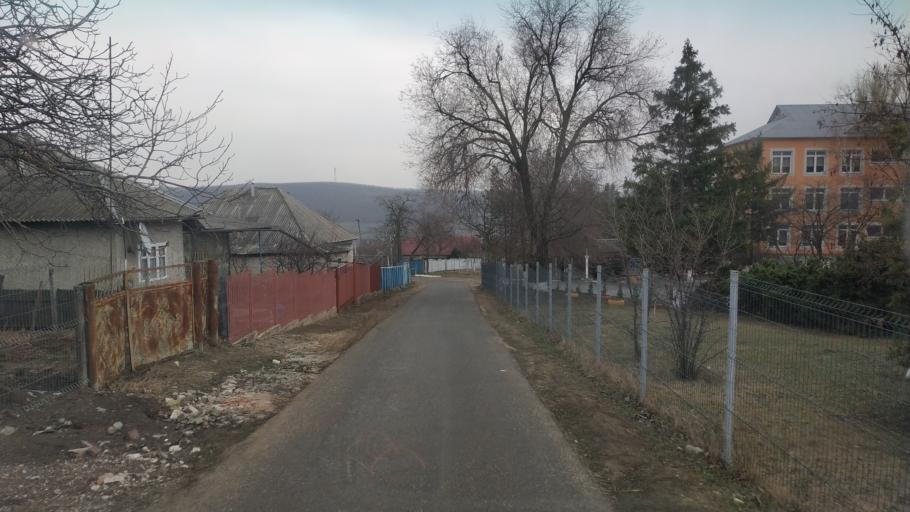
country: MD
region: Chisinau
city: Singera
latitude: 46.8317
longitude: 28.9709
